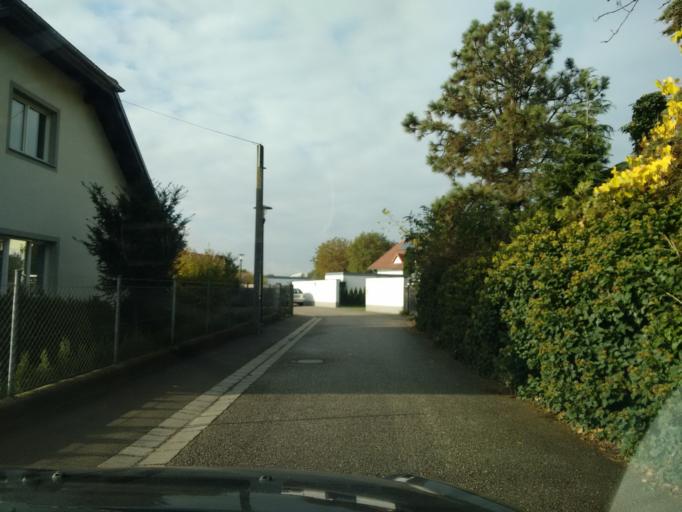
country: AT
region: Upper Austria
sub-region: Wels-Land
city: Gunskirchen
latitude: 48.1636
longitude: 13.9856
